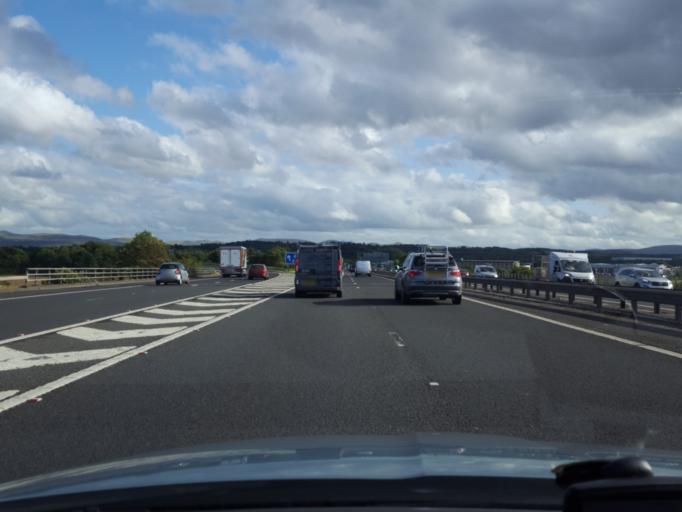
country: GB
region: Scotland
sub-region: Edinburgh
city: Kirkliston
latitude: 55.9449
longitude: -3.4060
